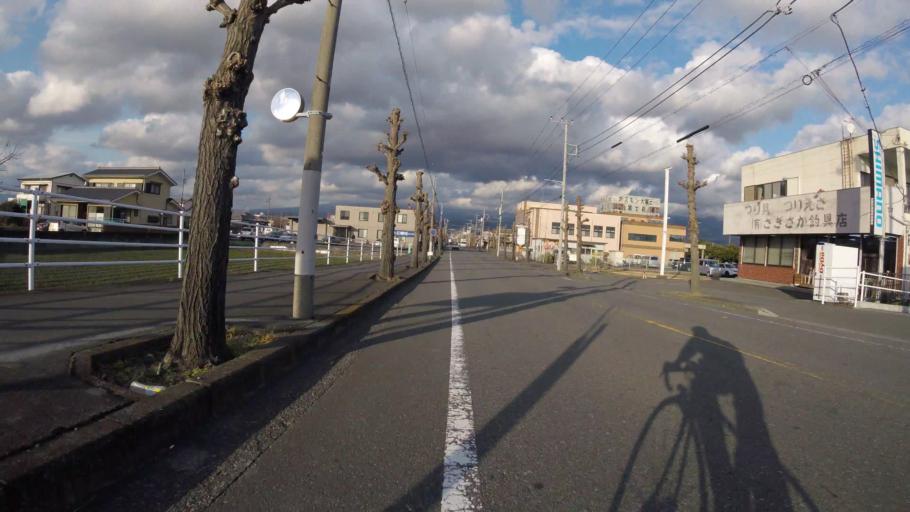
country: JP
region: Shizuoka
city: Fuji
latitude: 35.1522
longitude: 138.6825
